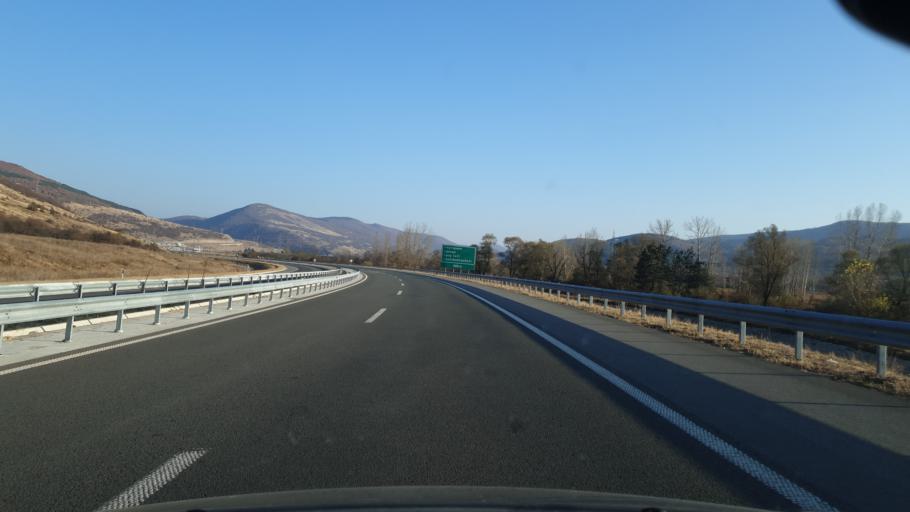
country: RS
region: Central Serbia
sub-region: Pirotski Okrug
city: Dimitrovgrad
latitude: 43.0245
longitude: 22.7262
